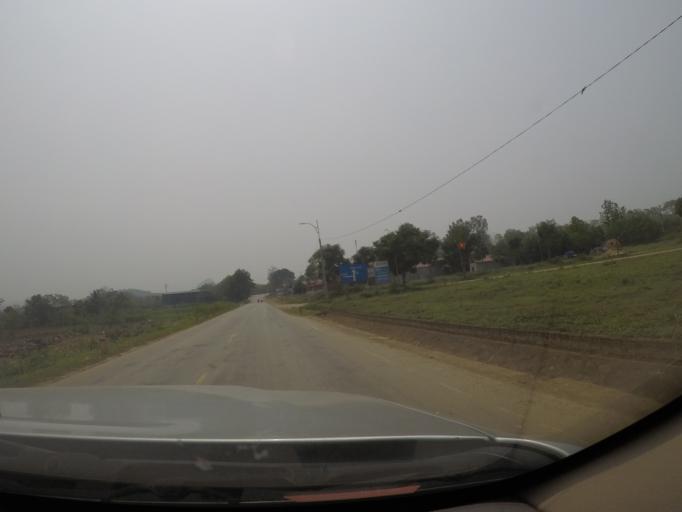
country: VN
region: Thanh Hoa
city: Thi Tran Thuong Xuan
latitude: 19.9472
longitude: 105.4034
